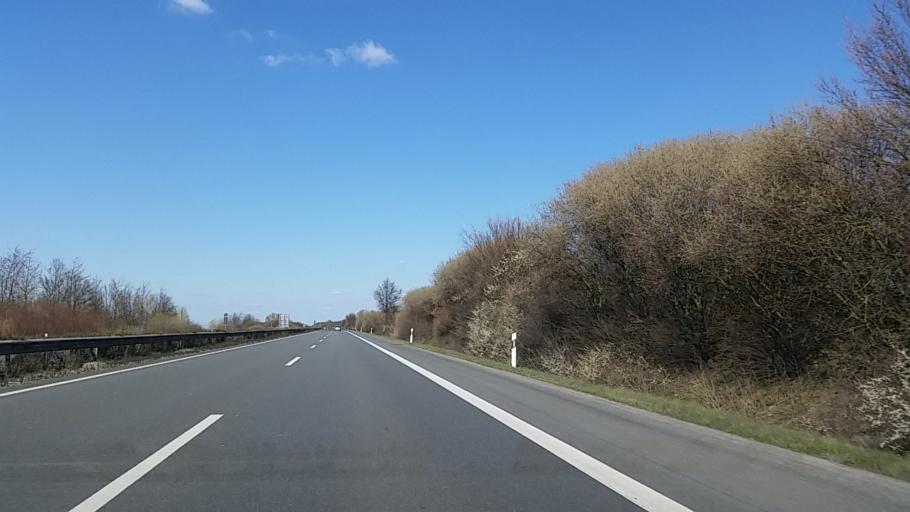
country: DE
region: Lower Saxony
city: Flothe
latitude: 52.0813
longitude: 10.4983
